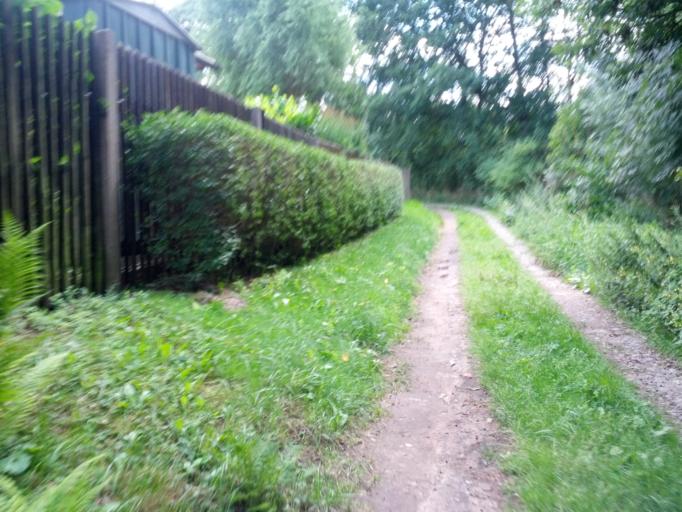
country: DE
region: Thuringia
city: Eisenach
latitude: 50.9854
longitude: 10.2920
